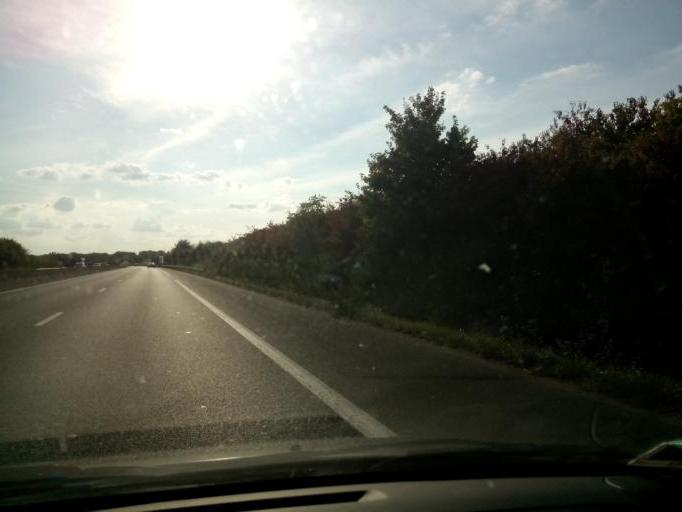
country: FR
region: Centre
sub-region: Departement d'Indre-et-Loire
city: Ballan-Mire
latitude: 47.3446
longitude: 0.6374
